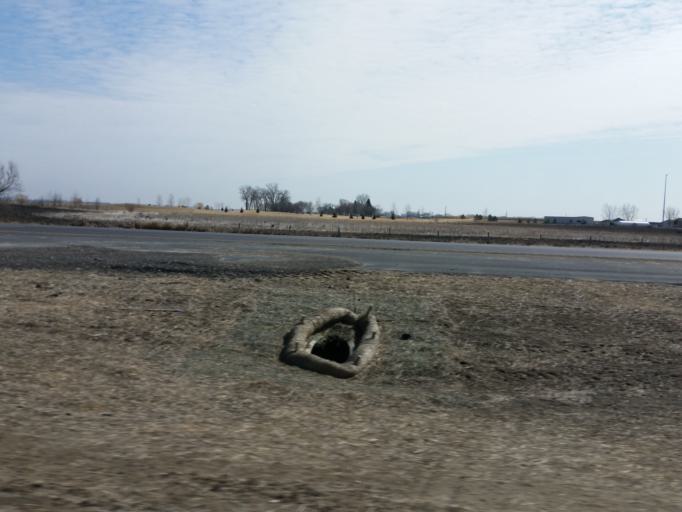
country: US
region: South Dakota
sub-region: Roberts County
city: Sisseton
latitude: 45.9430
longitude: -96.8393
